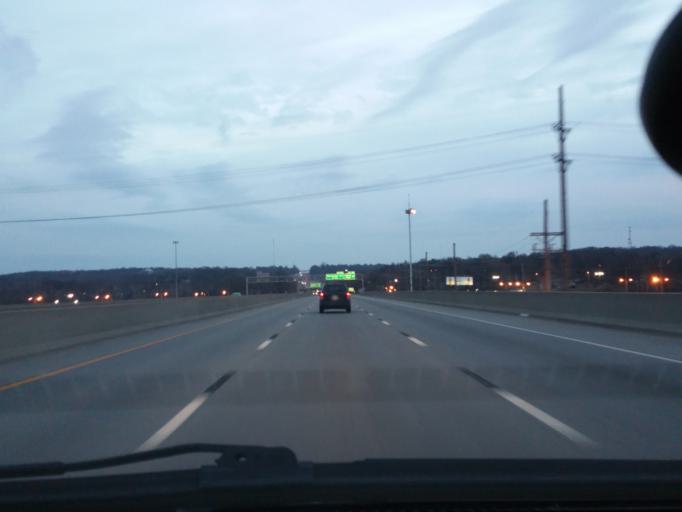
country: US
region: Kansas
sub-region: Johnson County
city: Shawnee
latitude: 39.0843
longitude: -94.6807
